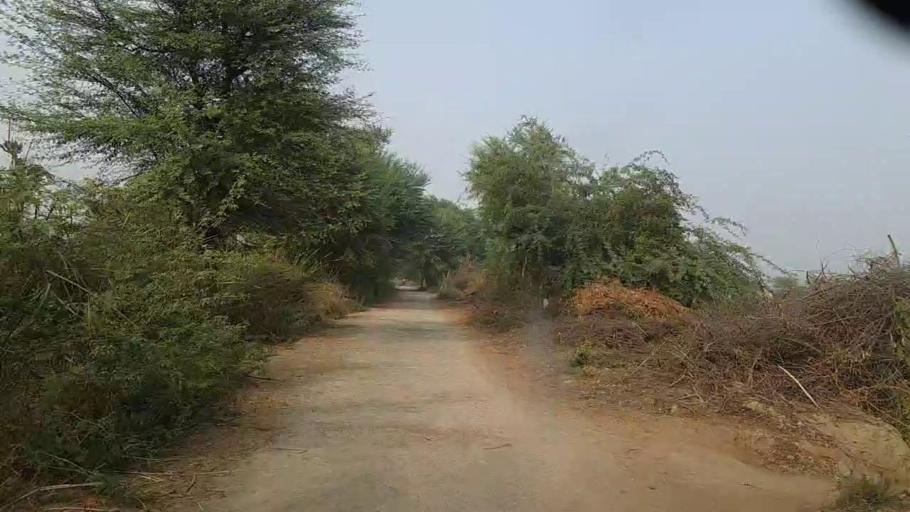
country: PK
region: Sindh
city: Bozdar
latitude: 27.1578
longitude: 68.6605
